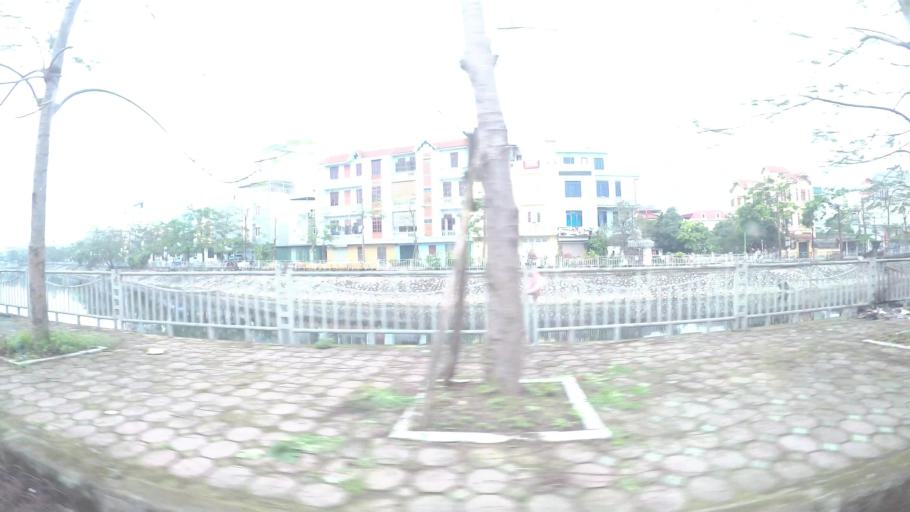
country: VN
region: Ha Noi
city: Van Dien
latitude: 20.9744
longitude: 105.8512
